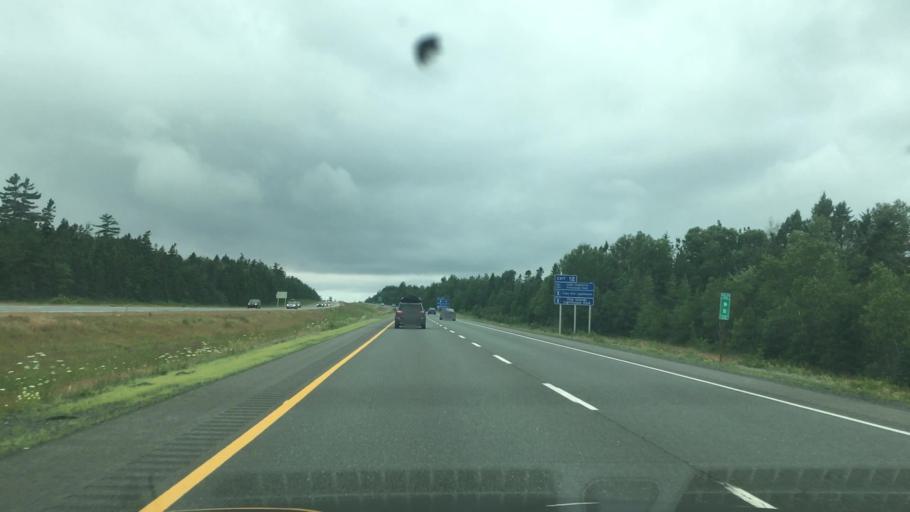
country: CA
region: Nova Scotia
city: Truro
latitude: 45.3978
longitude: -63.4624
